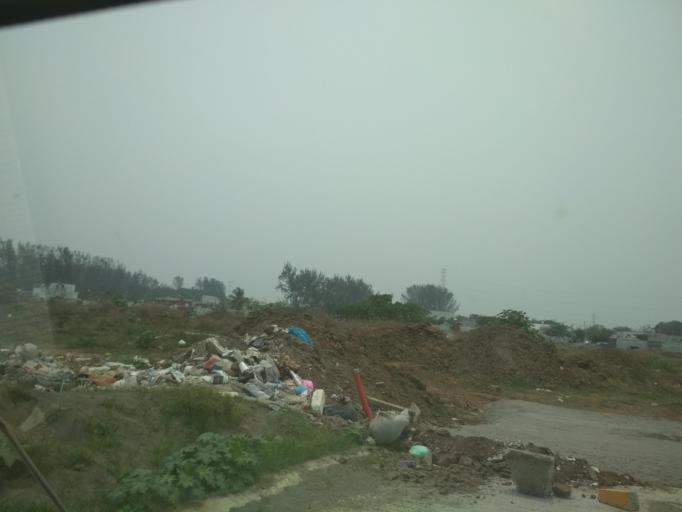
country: MX
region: Veracruz
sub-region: Veracruz
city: Las Amapolas
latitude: 19.1531
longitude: -96.2184
